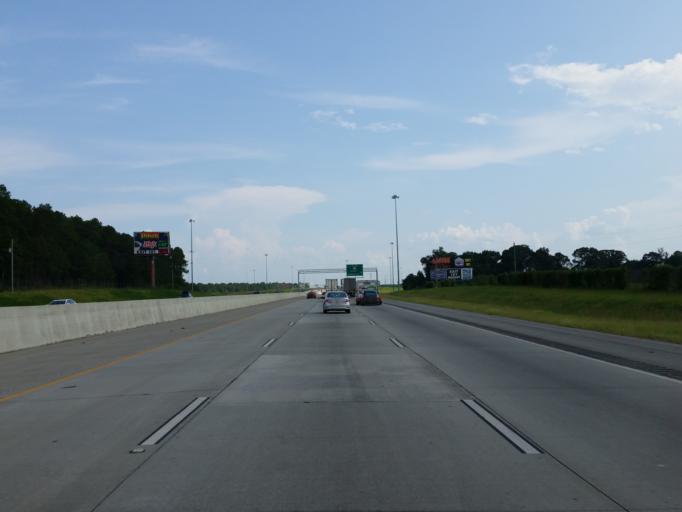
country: US
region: Georgia
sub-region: Crisp County
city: Cordele
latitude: 31.9829
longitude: -83.7553
